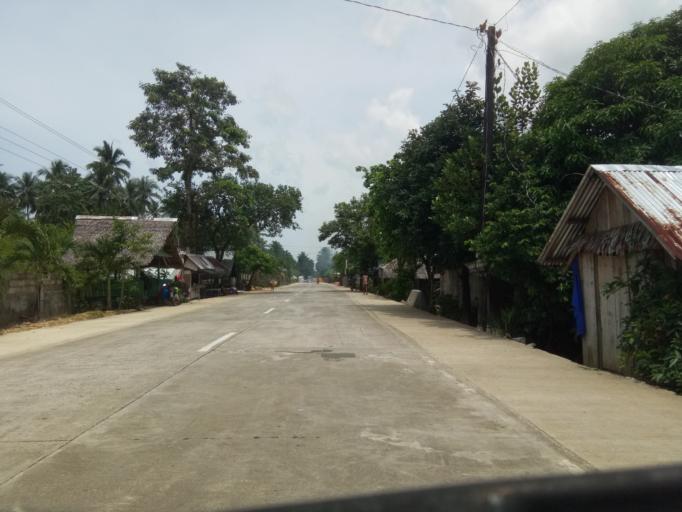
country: PH
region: Caraga
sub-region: Province of Surigao del Norte
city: San Isidro
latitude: 9.9172
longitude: 126.0463
